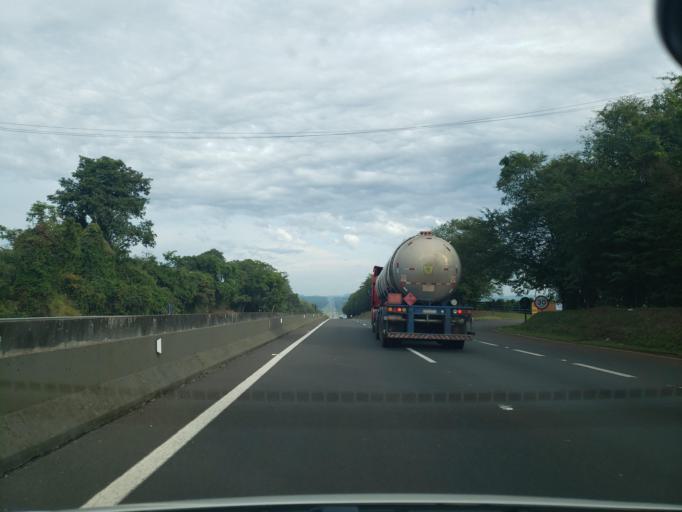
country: BR
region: Sao Paulo
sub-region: Itirapina
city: Itirapina
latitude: -22.2552
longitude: -47.8448
